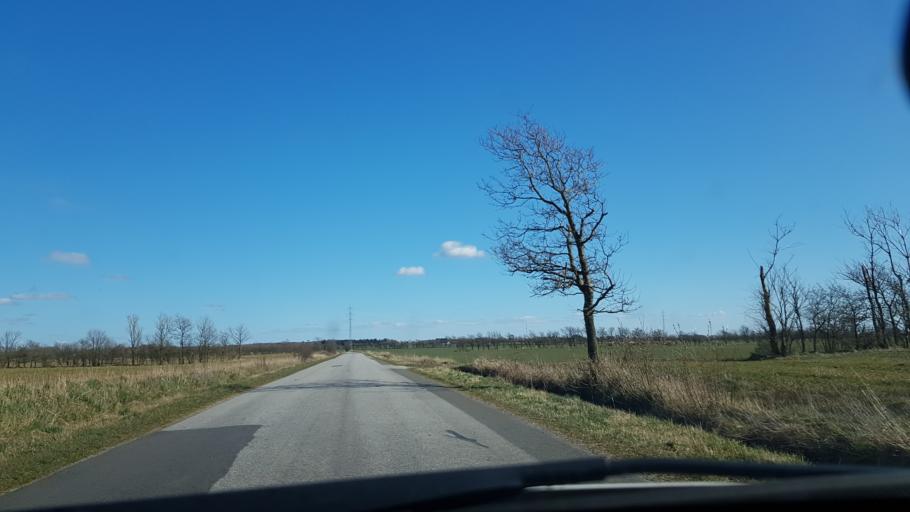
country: DK
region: South Denmark
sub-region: Tonder Kommune
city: Sherrebek
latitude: 55.2231
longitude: 8.8097
